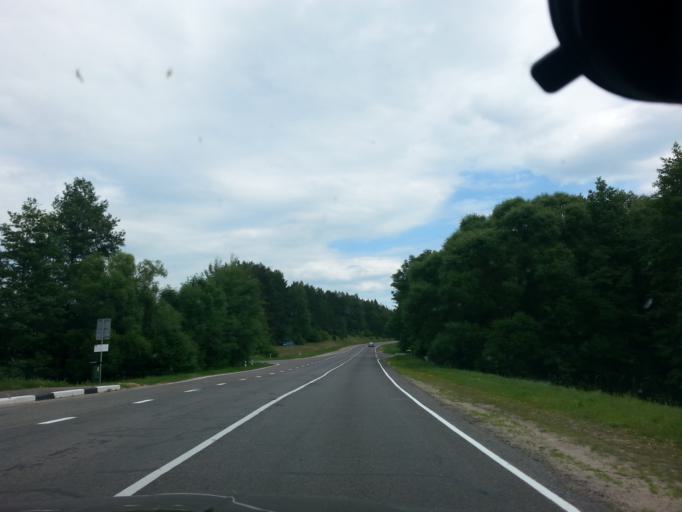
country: BY
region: Minsk
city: Narach
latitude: 54.8888
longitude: 26.7889
